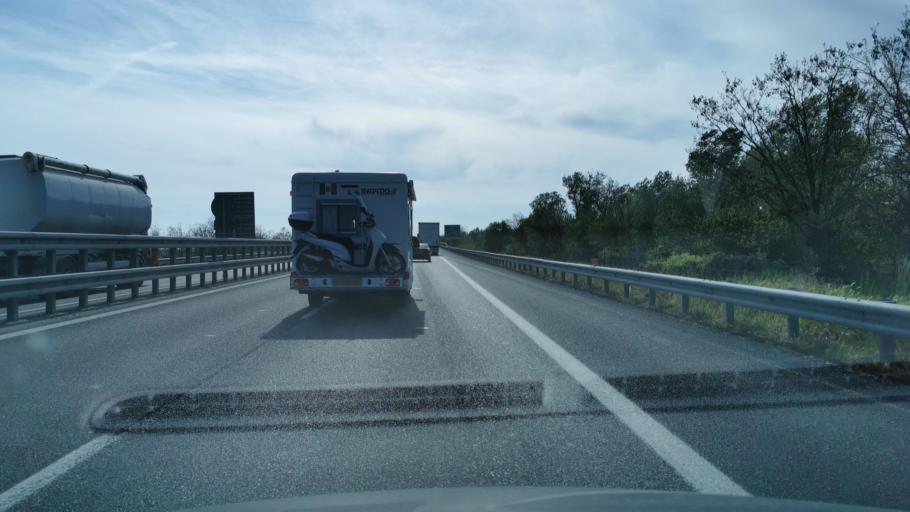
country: IT
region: Piedmont
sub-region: Provincia di Alessandria
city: Tortona
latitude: 44.9189
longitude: 8.8565
